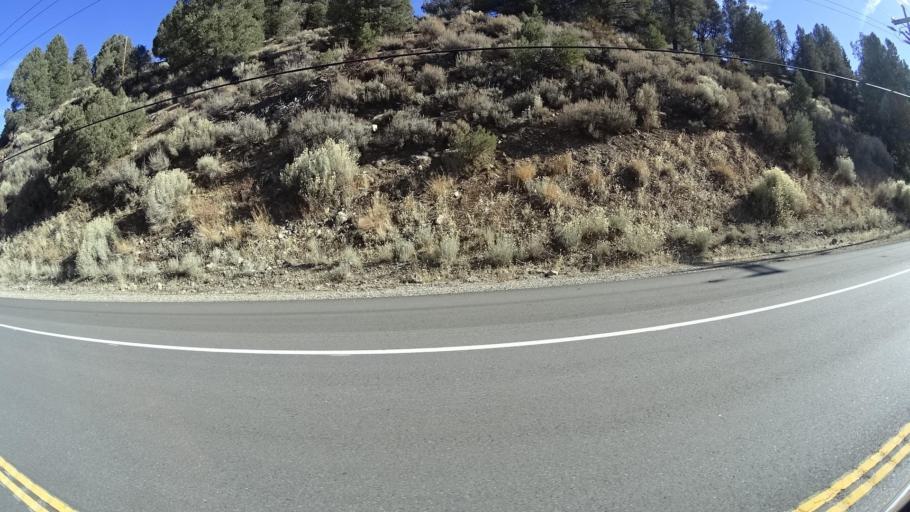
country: US
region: California
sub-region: Kern County
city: Frazier Park
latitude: 34.8115
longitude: -119.0114
